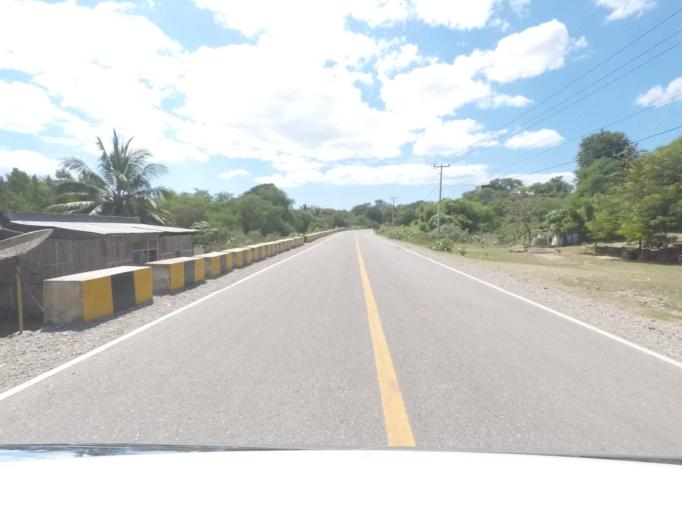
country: TL
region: Lautem
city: Lospalos
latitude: -8.3656
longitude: 126.8989
